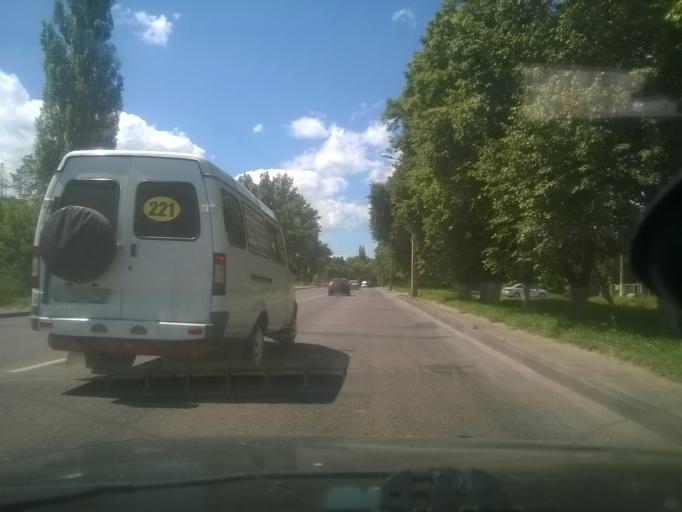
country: RU
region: Kursk
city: Voroshnevo
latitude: 51.6666
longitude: 36.1106
